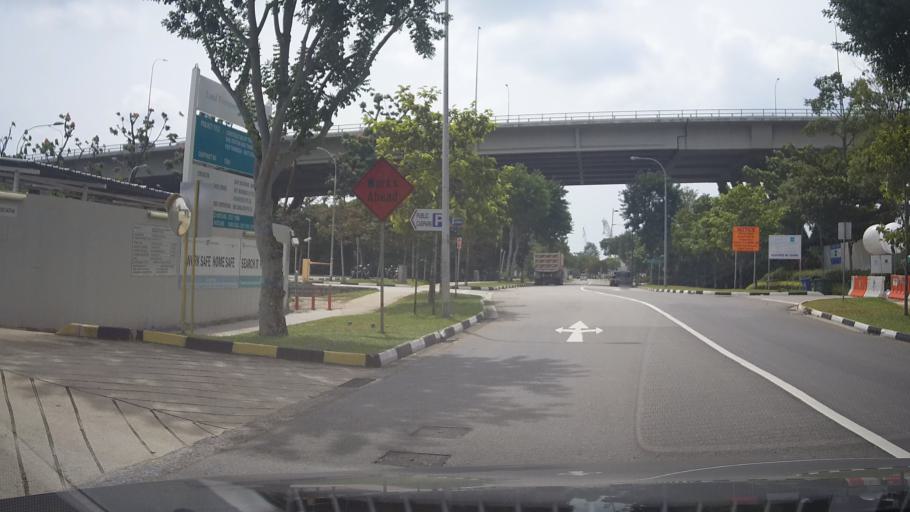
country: SG
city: Singapore
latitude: 1.2959
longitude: 103.8677
